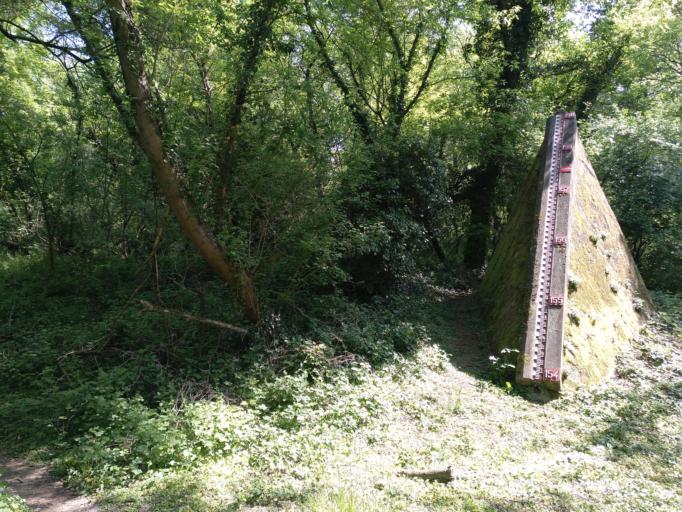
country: FR
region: Rhone-Alpes
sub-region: Departement du Rhone
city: Serezin-du-Rhone
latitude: 45.6270
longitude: 4.8086
